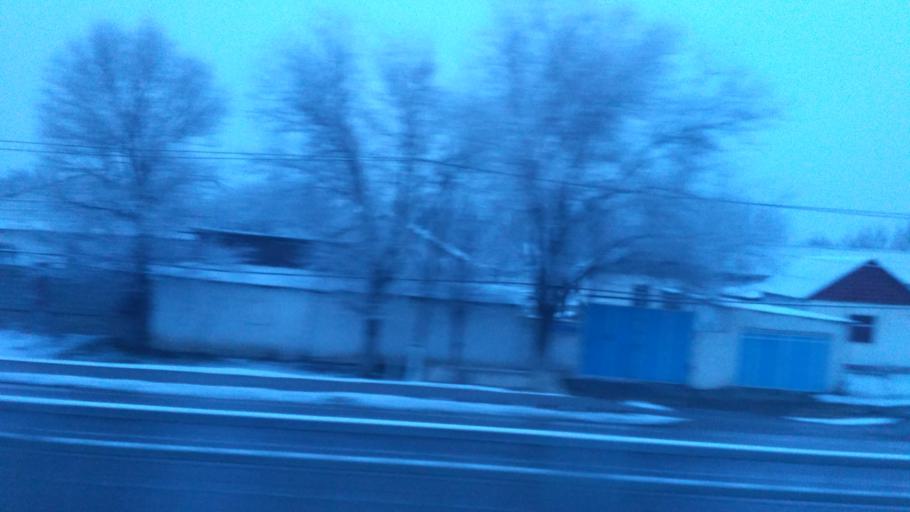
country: KZ
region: Ongtustik Qazaqstan
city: Shymkent
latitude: 42.3782
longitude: 69.4965
